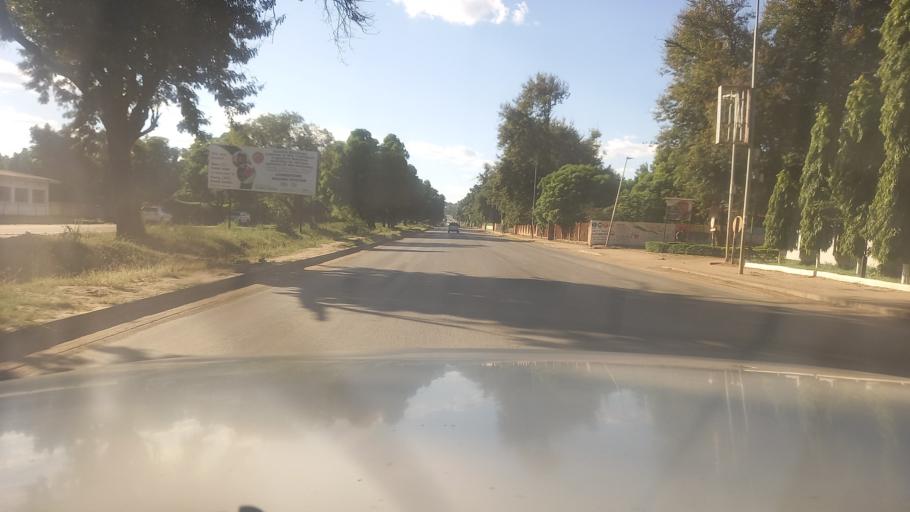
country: ZM
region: Southern
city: Livingstone
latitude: -17.8596
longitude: 25.8552
